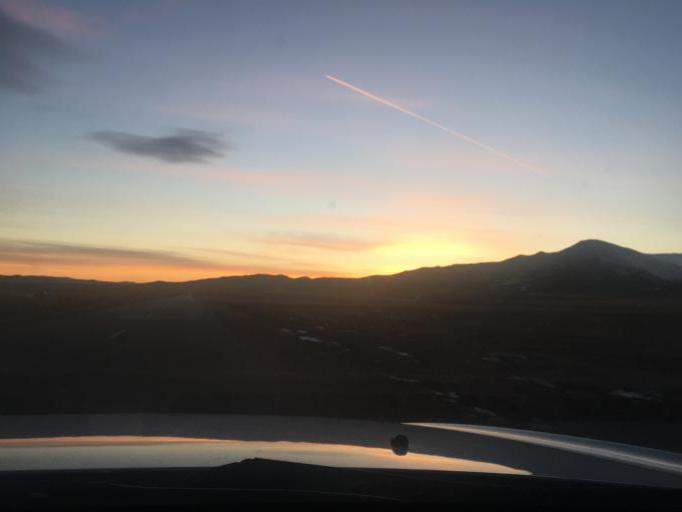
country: MN
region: Central Aimak
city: Mandal
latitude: 48.0907
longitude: 106.6023
